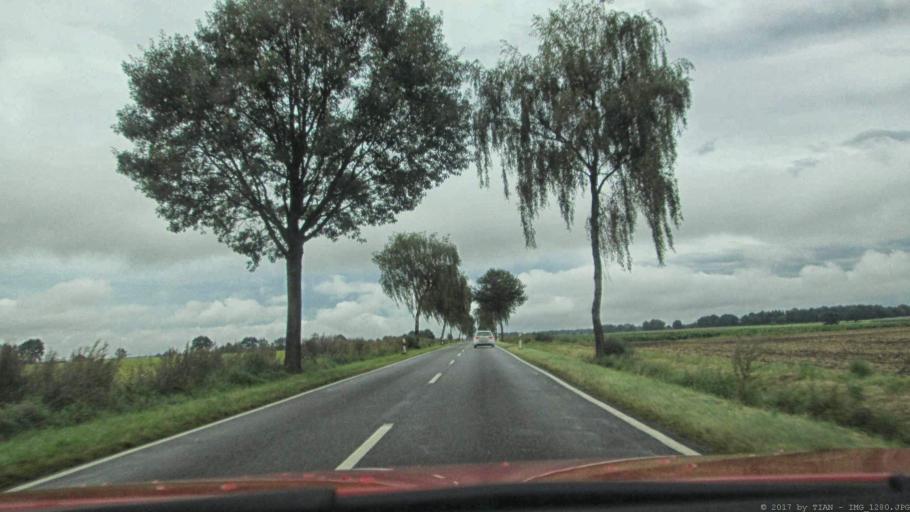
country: DE
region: Lower Saxony
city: Wittingen
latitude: 52.6789
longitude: 10.8024
